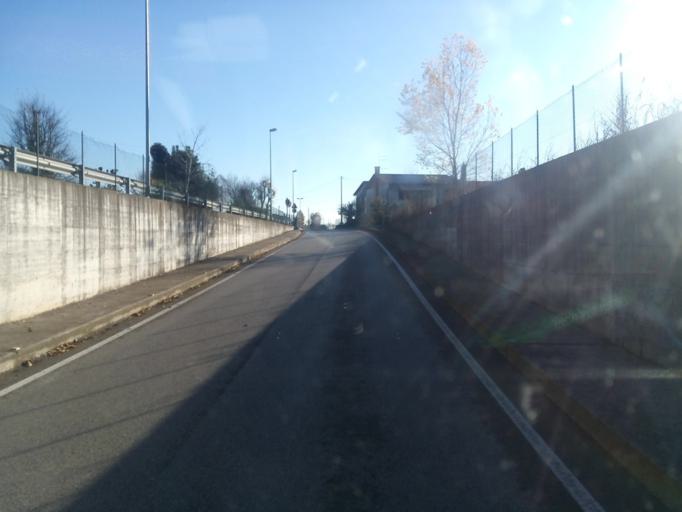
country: IT
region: Veneto
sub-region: Provincia di Padova
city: Loreggia
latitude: 45.6074
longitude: 11.9589
